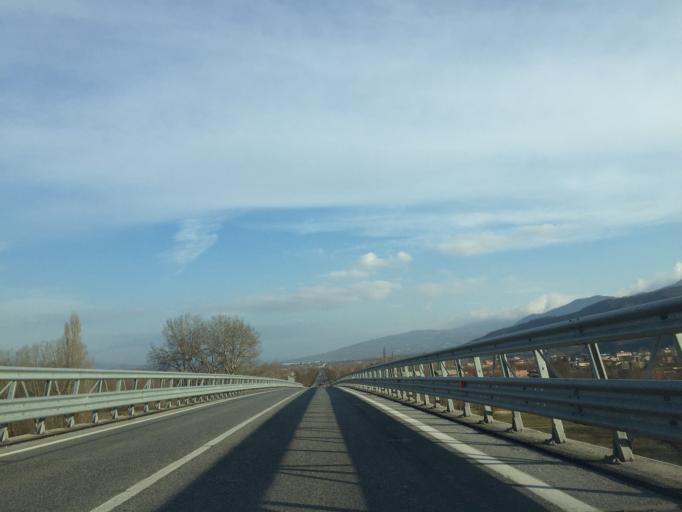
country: IT
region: Molise
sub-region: Provincia di Campobasso
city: Bojano
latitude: 41.4960
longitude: 14.4662
